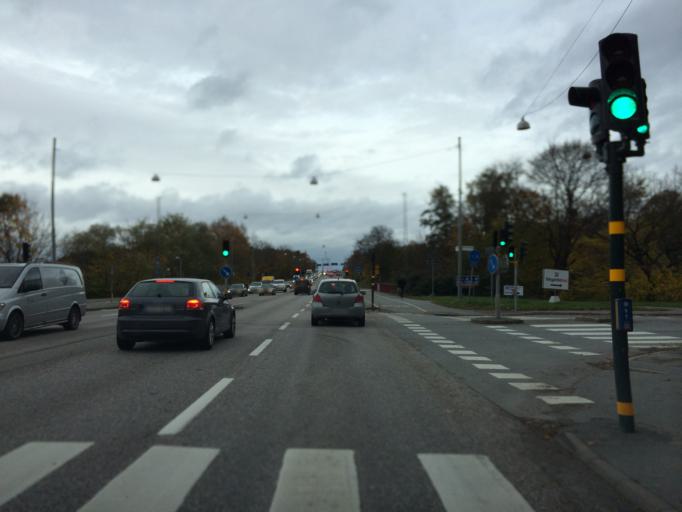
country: SE
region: Stockholm
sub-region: Stockholms Kommun
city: Bromma
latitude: 59.3407
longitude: 17.9620
